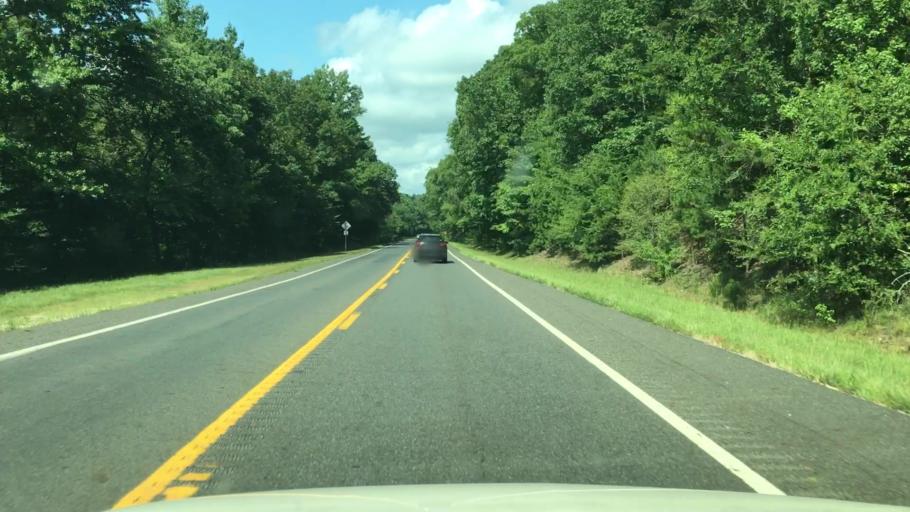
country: US
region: Arkansas
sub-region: Garland County
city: Lake Hamilton
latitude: 34.3621
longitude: -93.1659
